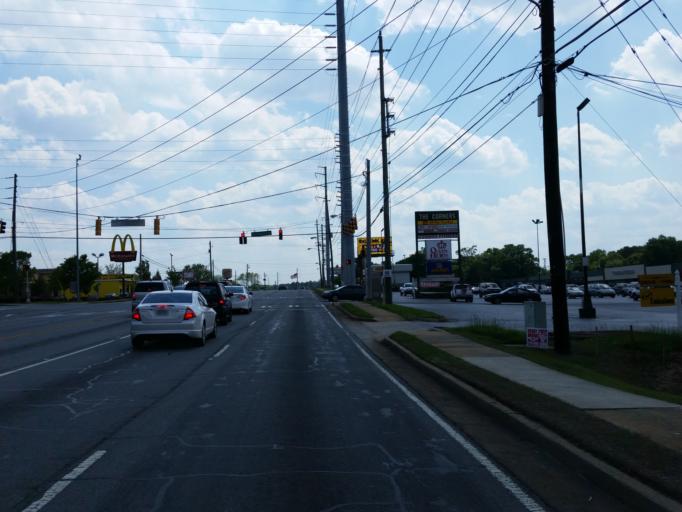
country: US
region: Georgia
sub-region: Cherokee County
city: Woodstock
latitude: 34.0184
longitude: -84.4913
